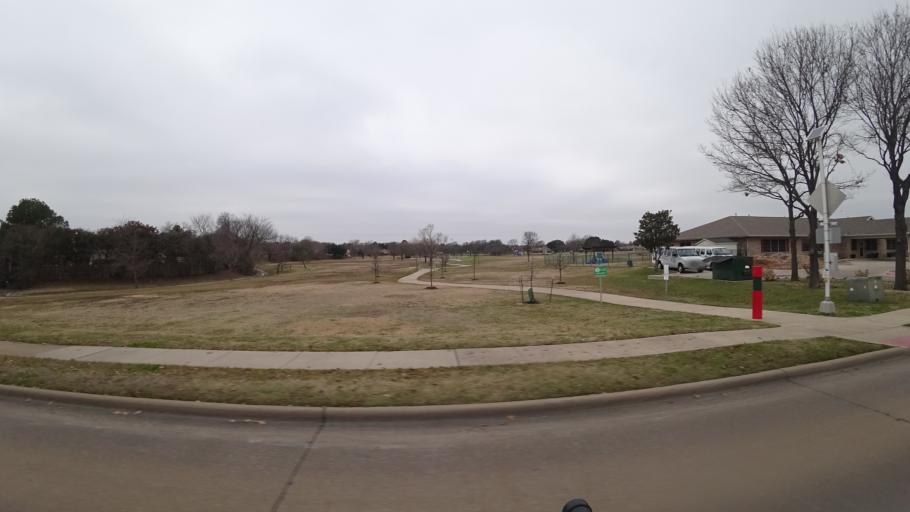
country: US
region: Texas
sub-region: Denton County
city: Highland Village
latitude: 33.0541
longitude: -97.0359
